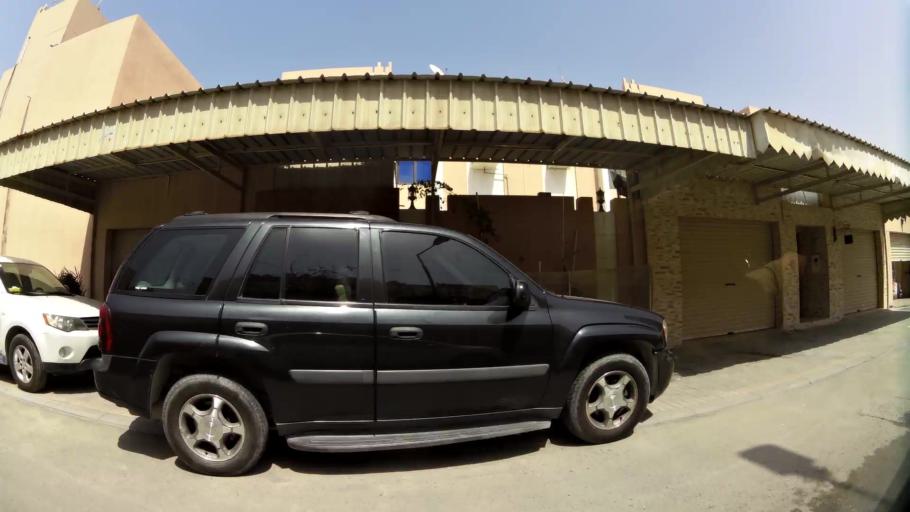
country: BH
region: Manama
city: Jidd Hafs
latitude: 26.2175
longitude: 50.4466
